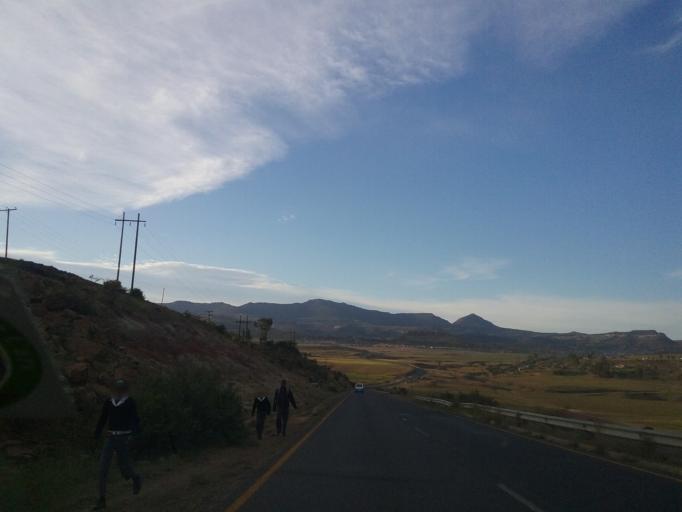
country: LS
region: Mohale's Hoek District
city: Mohale's Hoek
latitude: -30.1061
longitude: 27.4501
